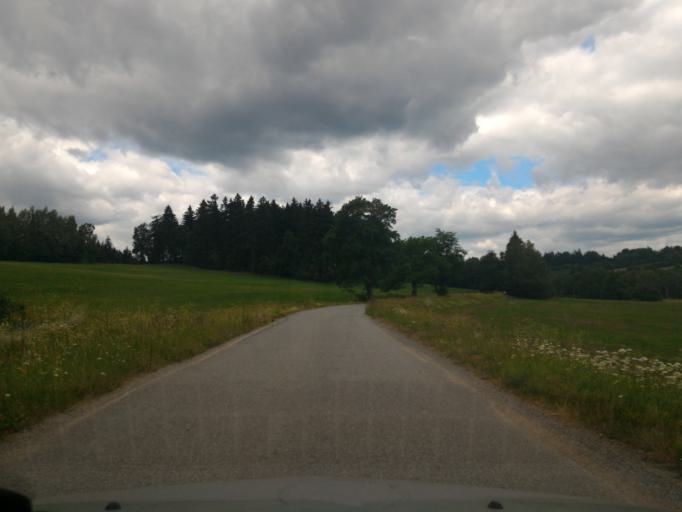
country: CZ
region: Vysocina
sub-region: Okres Jihlava
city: Telc
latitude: 49.2133
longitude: 15.4106
